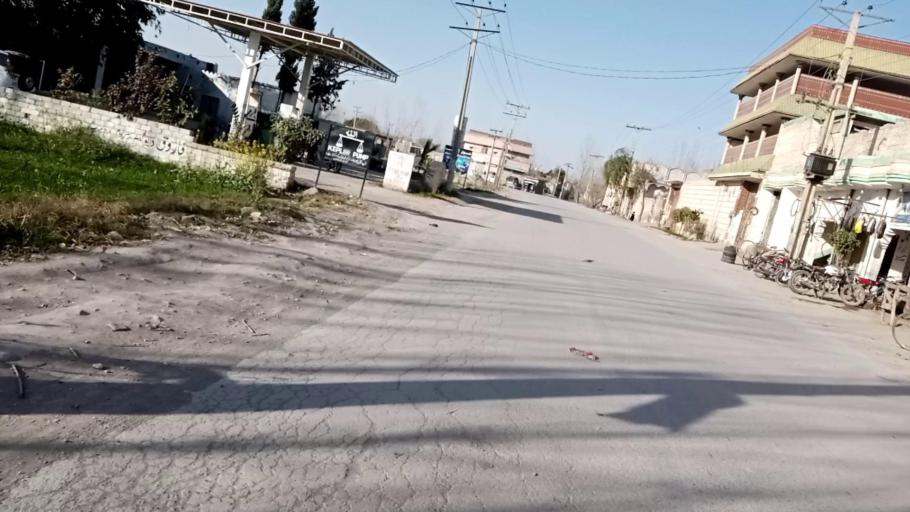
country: PK
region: Khyber Pakhtunkhwa
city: Peshawar
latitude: 34.0689
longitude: 71.5385
